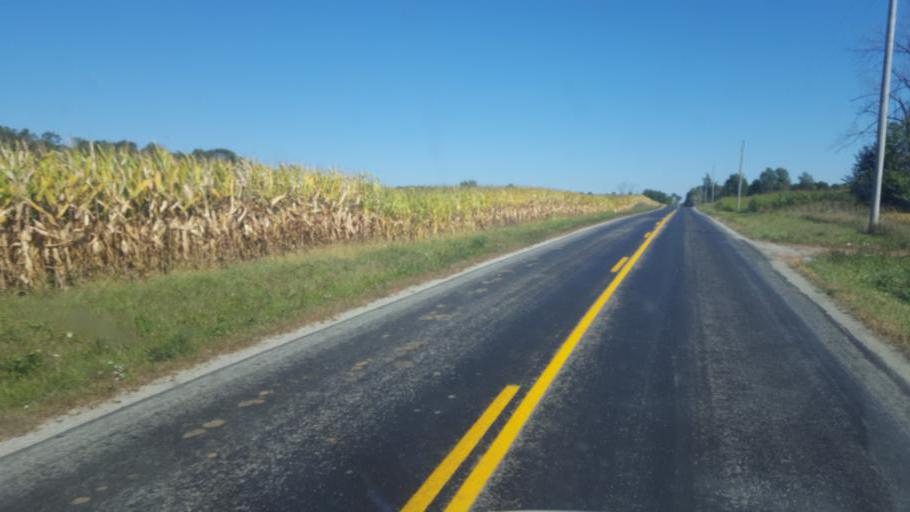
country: US
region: Ohio
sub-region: Wayne County
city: West Salem
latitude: 40.9922
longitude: -82.2114
